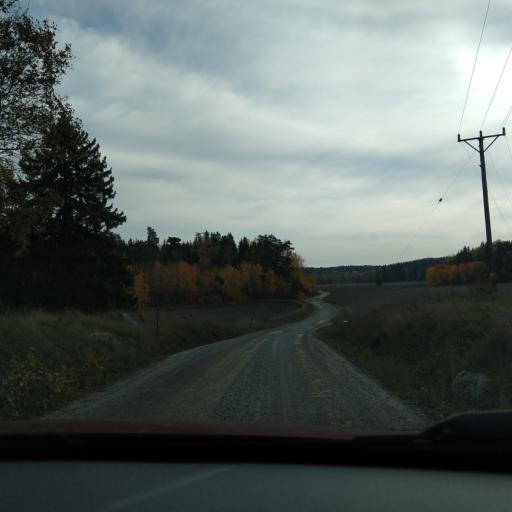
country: SE
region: Stockholm
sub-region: Vallentuna Kommun
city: Vallentuna
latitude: 59.5417
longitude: 18.0179
